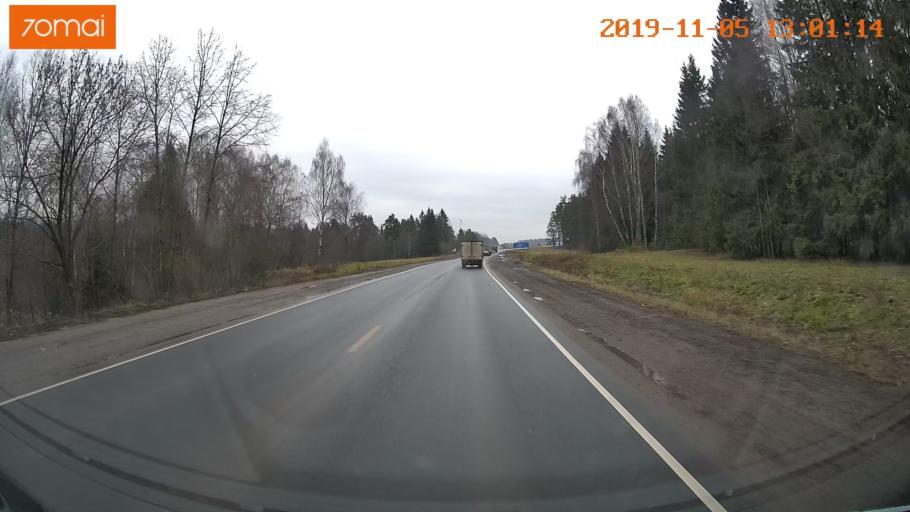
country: RU
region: Ivanovo
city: Kokhma
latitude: 56.9100
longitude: 41.1588
